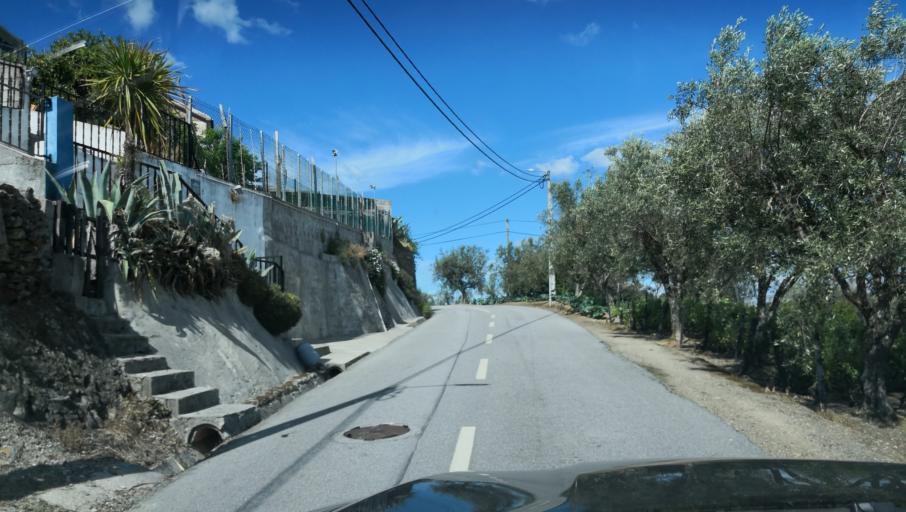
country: PT
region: Vila Real
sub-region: Vila Real
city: Vila Real
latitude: 41.2542
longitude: -7.7339
